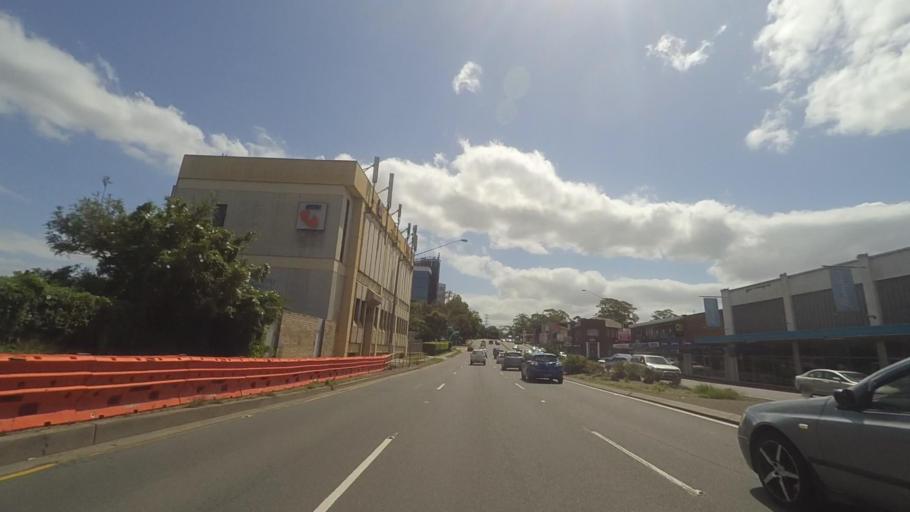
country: AU
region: New South Wales
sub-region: Hornsby Shire
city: Pennant Hills
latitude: -33.7392
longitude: 151.0710
